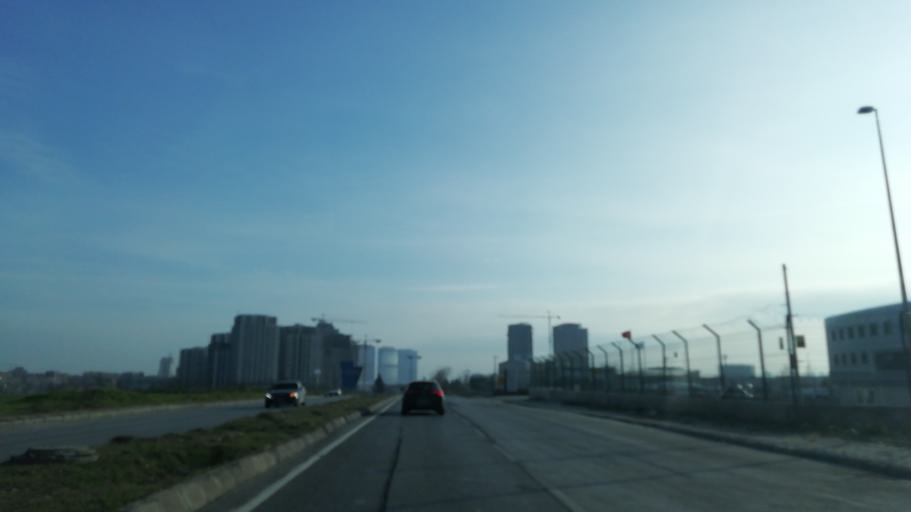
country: TR
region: Istanbul
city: Esenyurt
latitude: 41.0799
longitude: 28.6531
